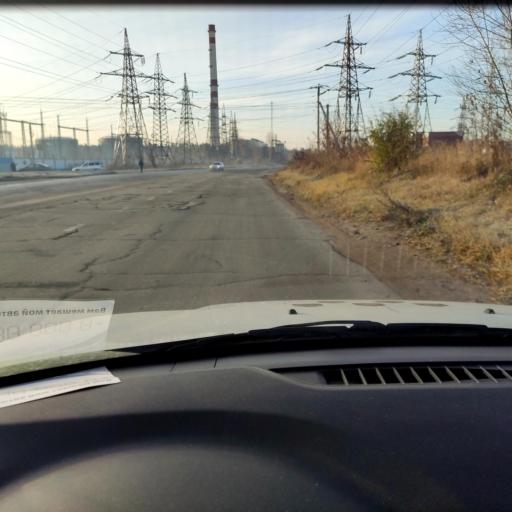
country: RU
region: Samara
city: Tol'yatti
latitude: 53.5167
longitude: 49.4657
